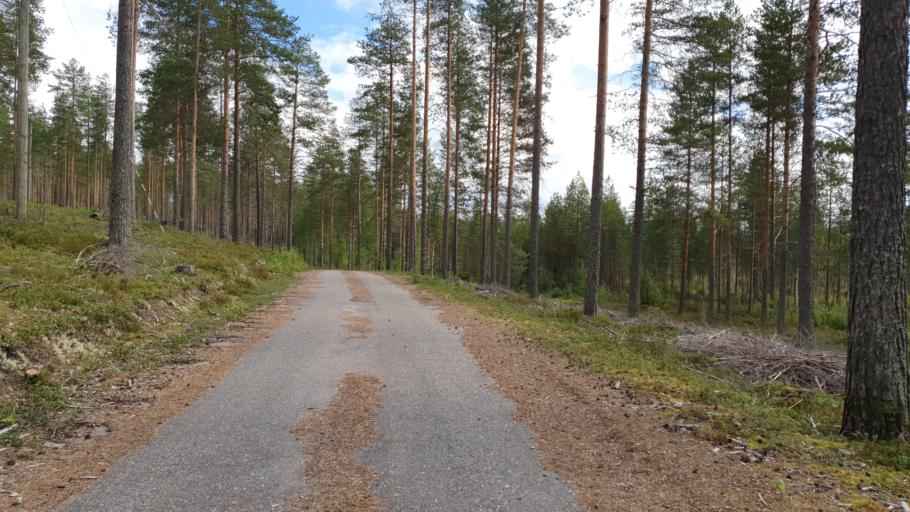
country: FI
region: Kainuu
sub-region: Kehys-Kainuu
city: Kuhmo
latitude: 64.1171
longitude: 29.5766
